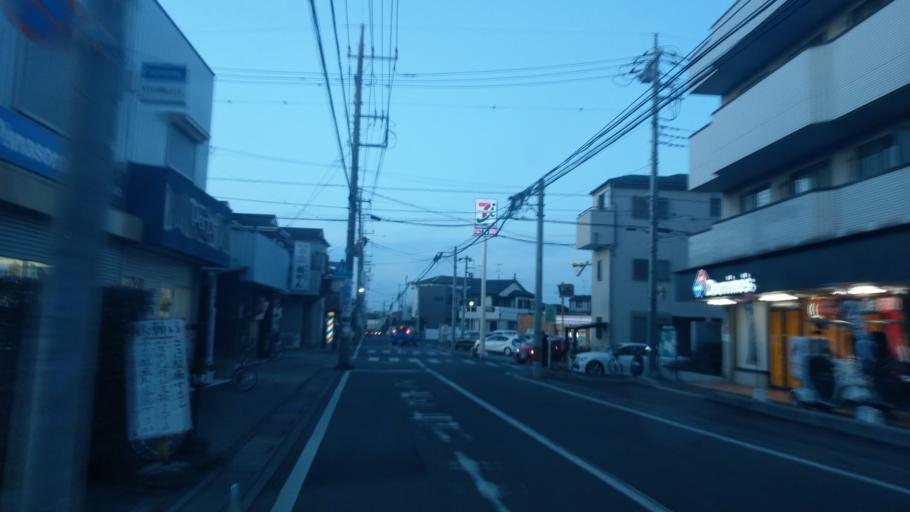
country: JP
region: Saitama
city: Yono
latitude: 35.8842
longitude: 139.6045
